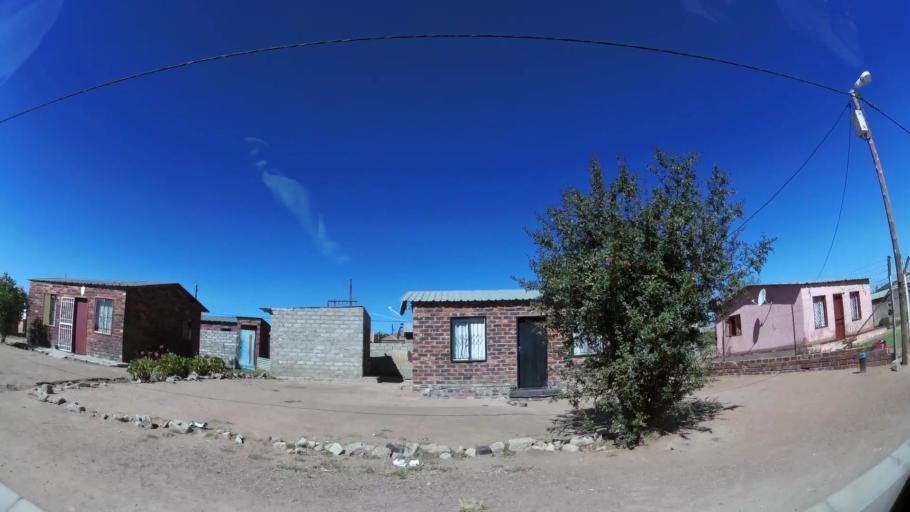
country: ZA
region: Limpopo
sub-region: Capricorn District Municipality
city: Polokwane
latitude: -23.8486
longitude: 29.4111
